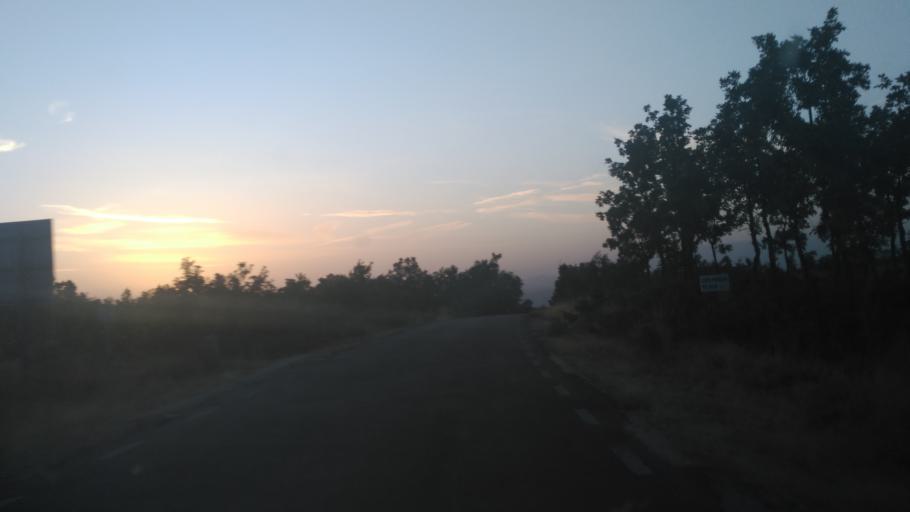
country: ES
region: Castille and Leon
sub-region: Provincia de Salamanca
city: Nava de Francia
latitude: 40.5230
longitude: -6.1088
